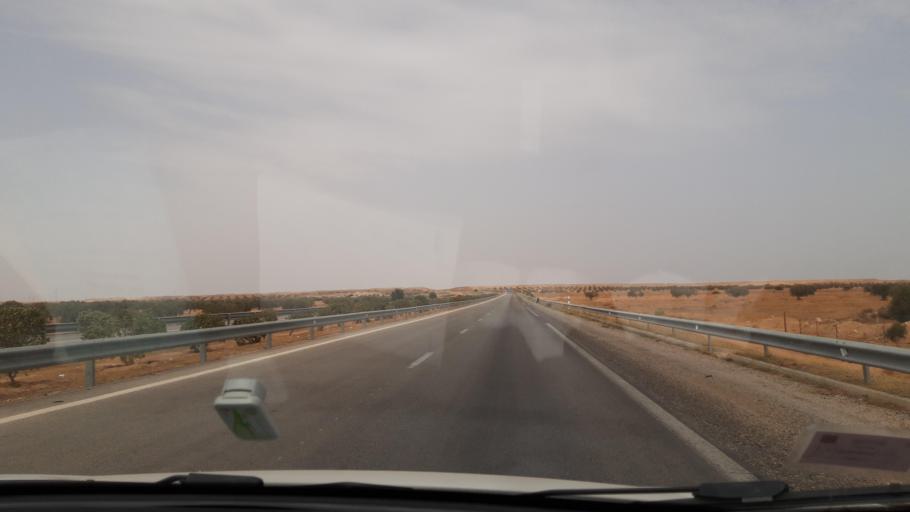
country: TN
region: Safaqis
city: Sfax
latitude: 34.7452
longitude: 10.6005
